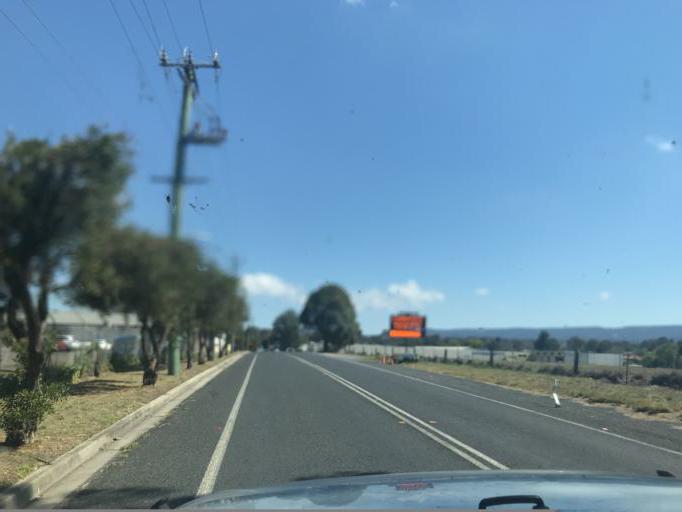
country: AU
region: New South Wales
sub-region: Hawkesbury
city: Richmond
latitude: -33.5780
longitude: 150.7233
